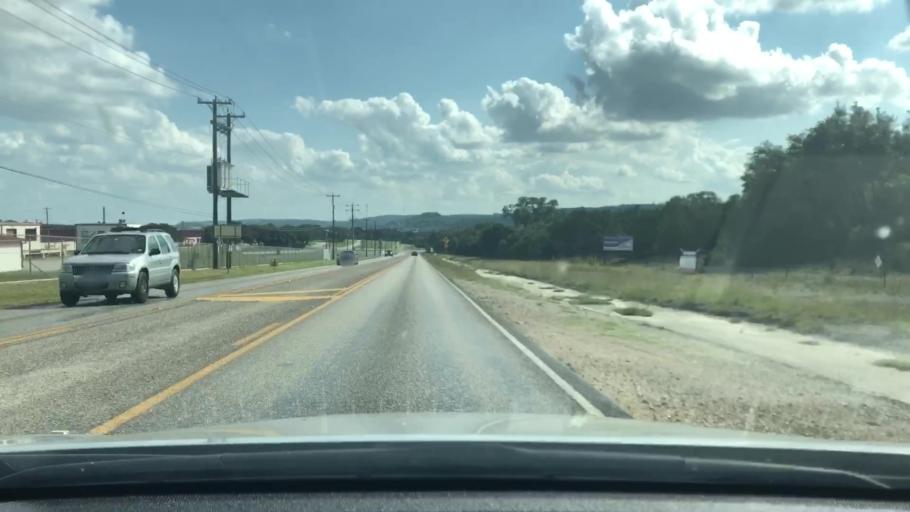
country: US
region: Texas
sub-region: Bexar County
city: Cross Mountain
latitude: 29.6838
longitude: -98.6316
